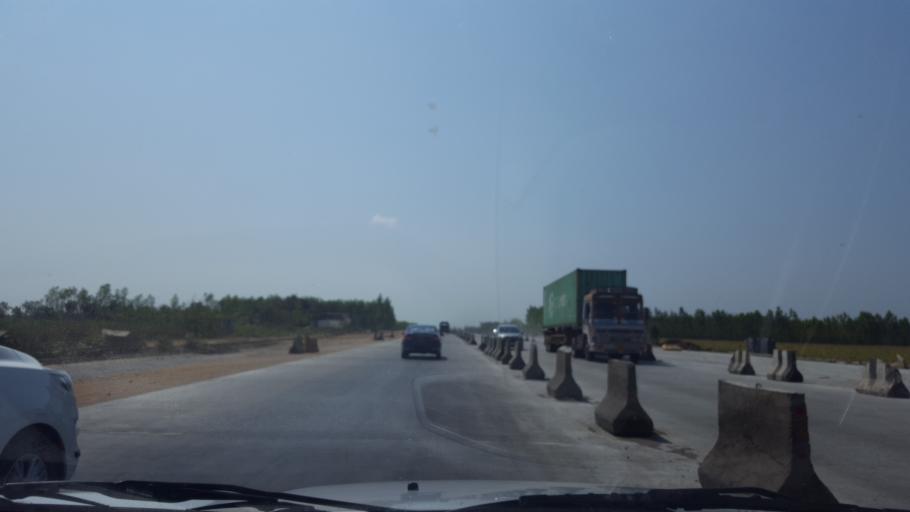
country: IN
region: Andhra Pradesh
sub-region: Prakasam
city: Addanki
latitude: 15.8002
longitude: 80.0400
